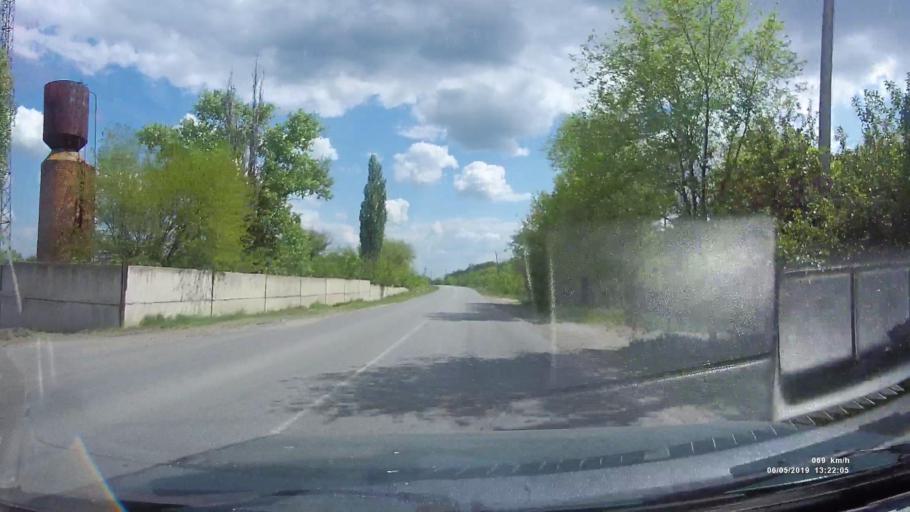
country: RU
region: Rostov
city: Ust'-Donetskiy
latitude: 47.6989
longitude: 40.9158
